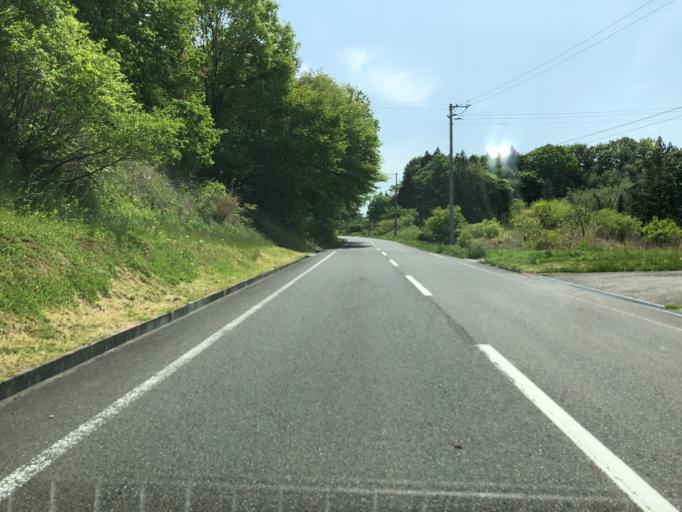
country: JP
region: Fukushima
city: Ishikawa
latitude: 37.1884
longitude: 140.5345
